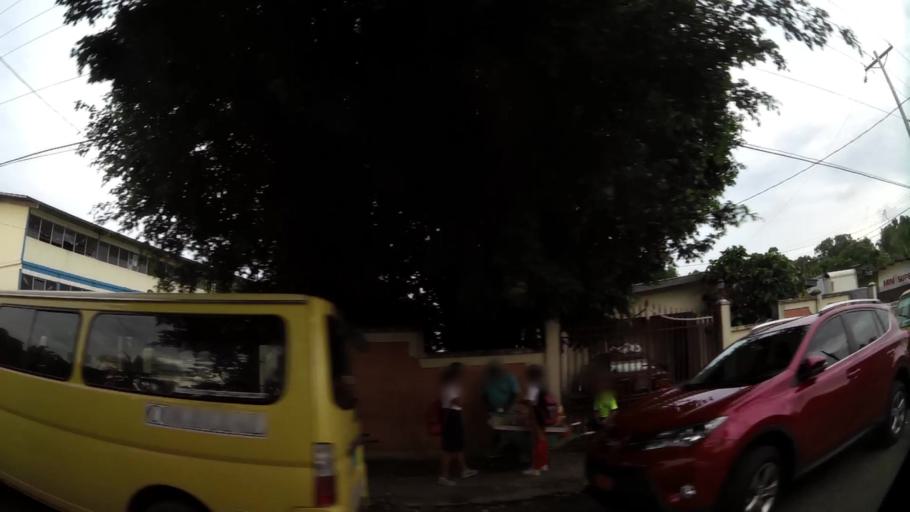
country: PA
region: Panama
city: Tocumen
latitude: 9.0897
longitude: -79.3941
